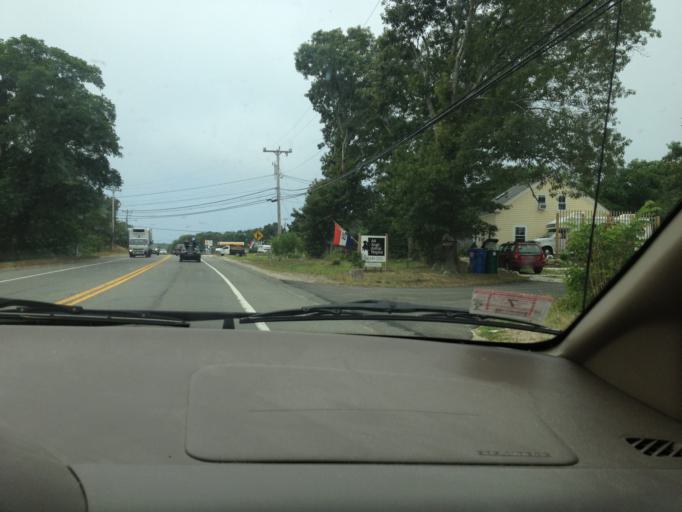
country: US
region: Massachusetts
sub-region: Barnstable County
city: Wellfleet
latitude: 41.9168
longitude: -69.9918
